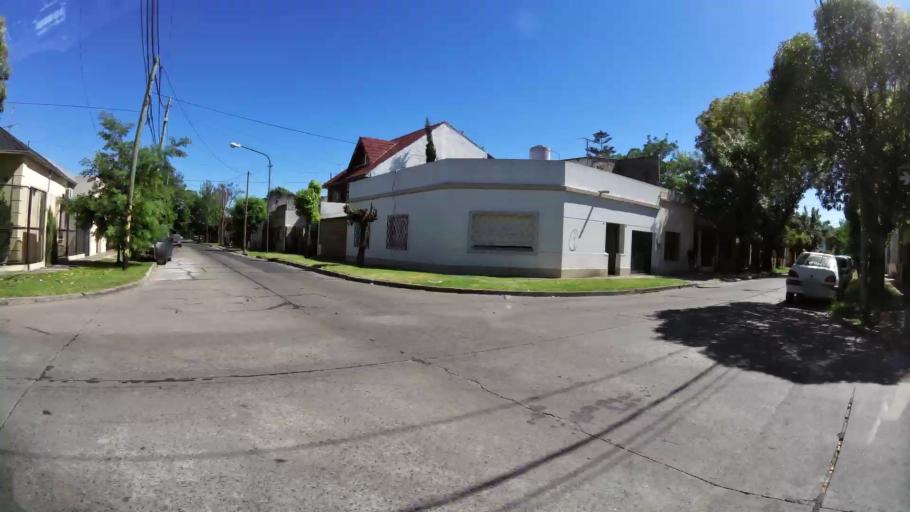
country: AR
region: Buenos Aires
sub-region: Partido de General San Martin
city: General San Martin
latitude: -34.5259
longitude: -58.5311
